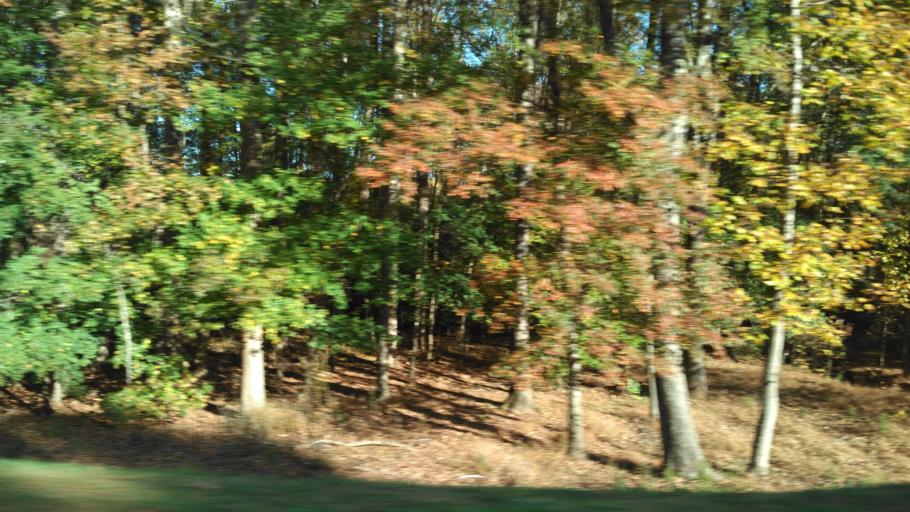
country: US
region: South Carolina
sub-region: Greenville County
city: Greer
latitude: 34.8842
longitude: -82.2156
